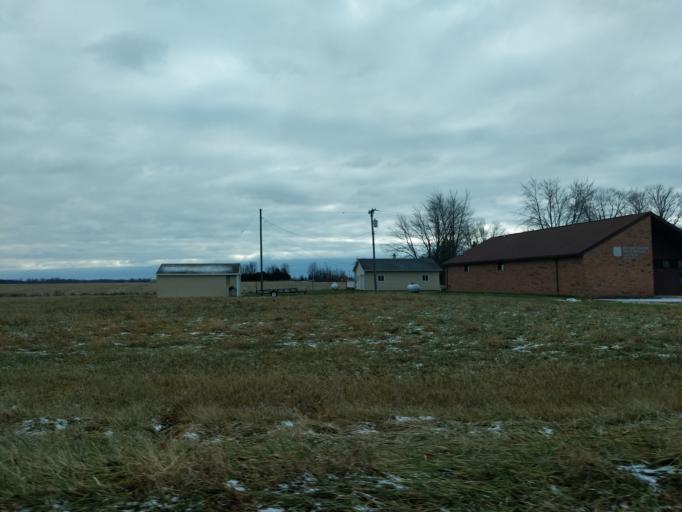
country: US
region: Michigan
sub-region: Lapeer County
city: North Branch
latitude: 43.3231
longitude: -83.2471
